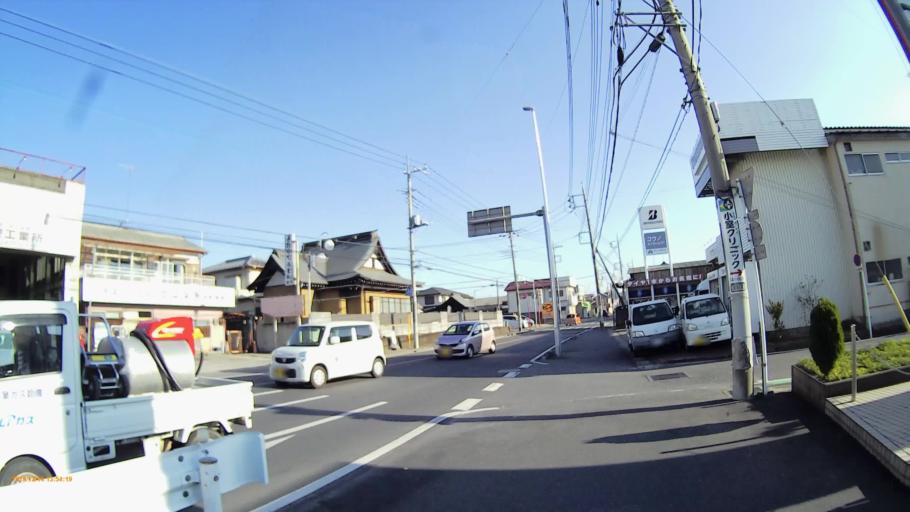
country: JP
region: Saitama
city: Konosu
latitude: 36.0663
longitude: 139.5059
